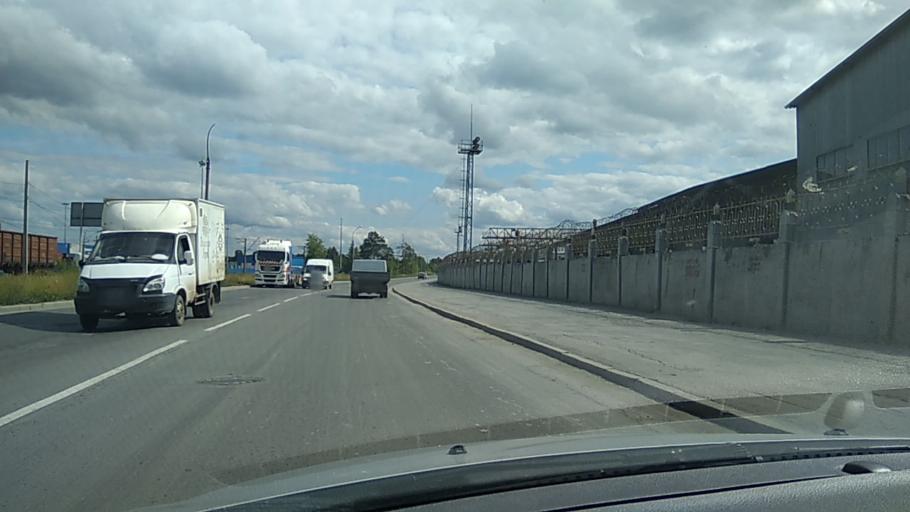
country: RU
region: Sverdlovsk
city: Shuvakish
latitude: 56.8874
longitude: 60.5380
